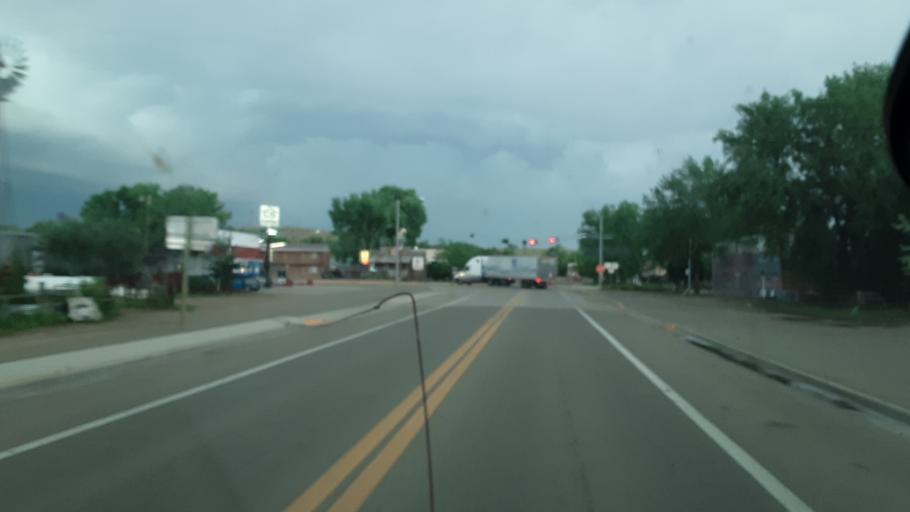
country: US
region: Montana
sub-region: Powder River County
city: Broadus
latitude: 45.4425
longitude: -105.4083
